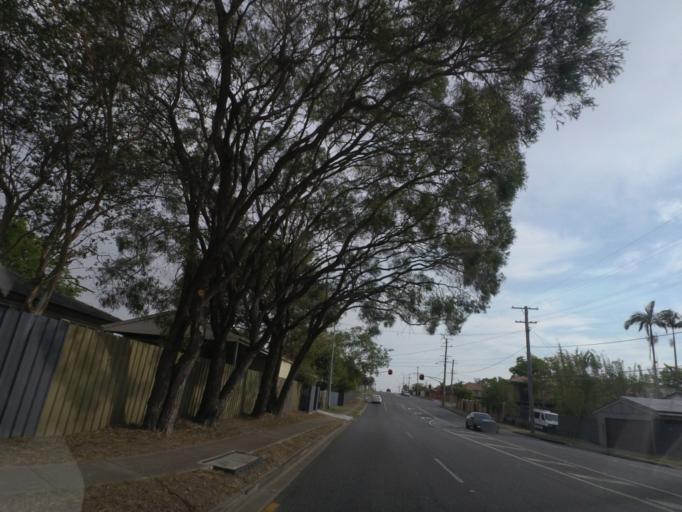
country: AU
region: Queensland
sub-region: Brisbane
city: Coopers Plains
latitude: -27.5532
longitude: 153.0415
